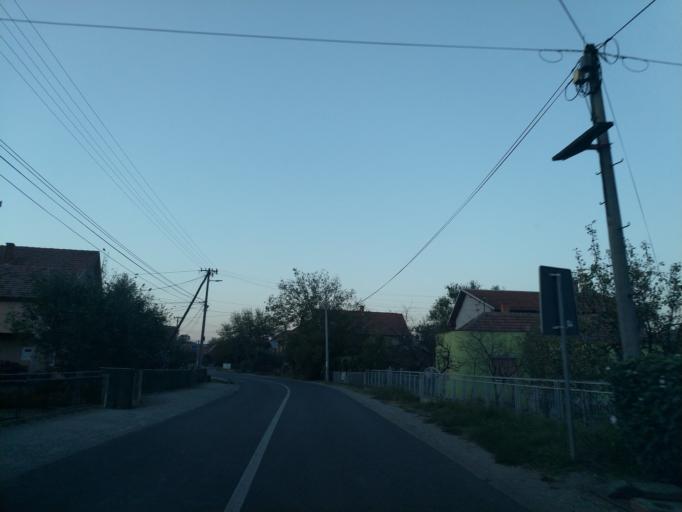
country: RS
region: Central Serbia
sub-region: Rasinski Okrug
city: Krusevac
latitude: 43.6131
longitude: 21.2968
